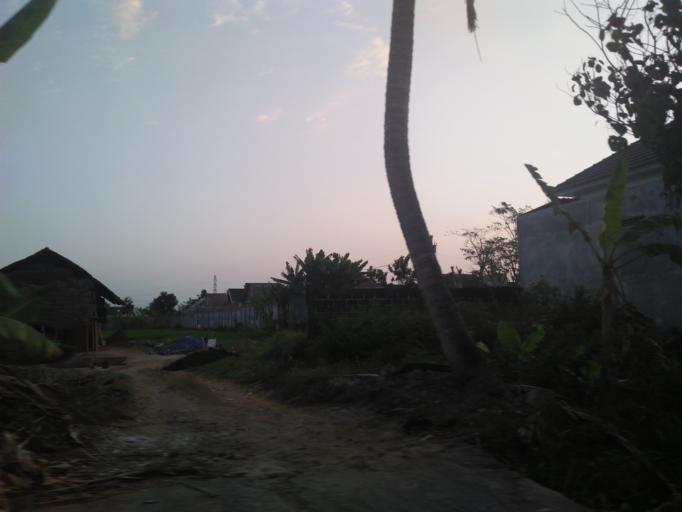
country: ID
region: Daerah Istimewa Yogyakarta
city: Sewon
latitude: -7.8461
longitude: 110.4048
